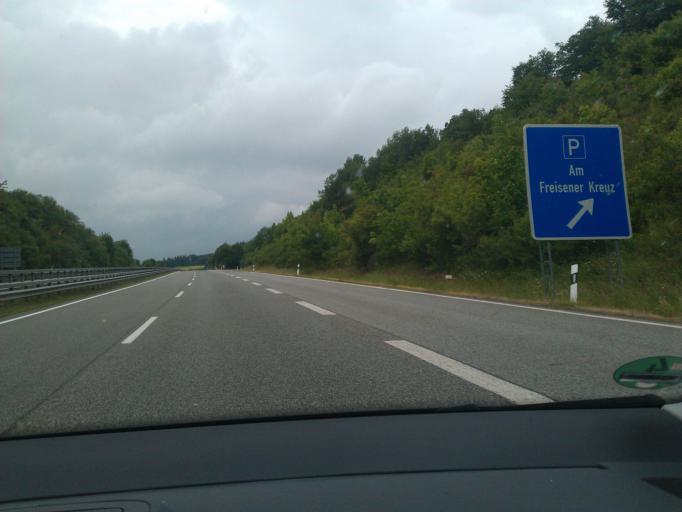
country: DE
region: Saarland
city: Freisen
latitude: 49.5675
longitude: 7.2560
